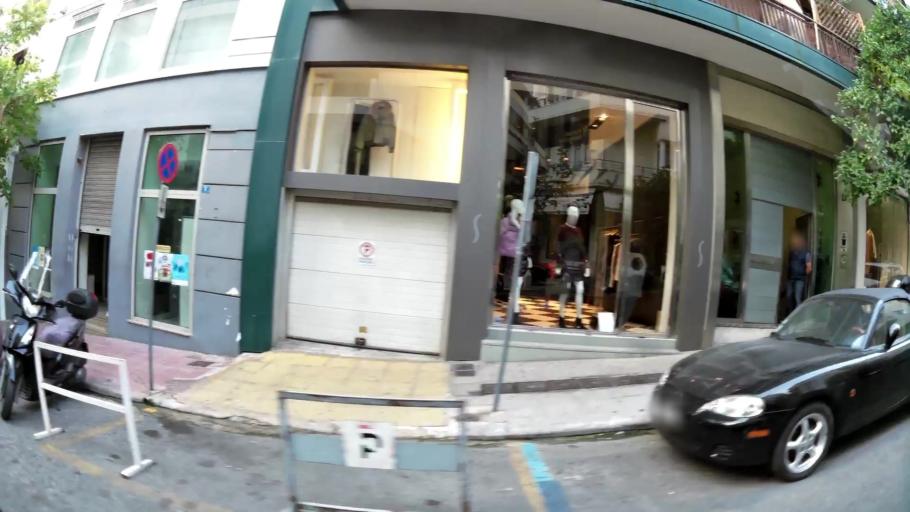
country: GR
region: Attica
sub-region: Nomarchia Athinas
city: Vyronas
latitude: 37.9778
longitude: 23.7412
